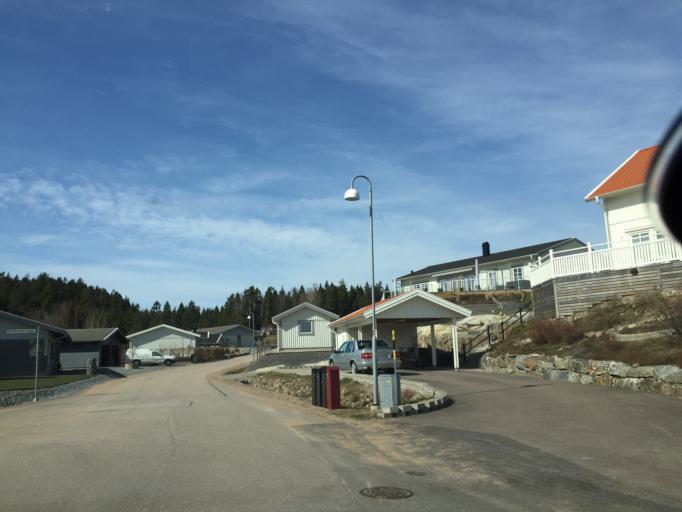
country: SE
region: Vaestra Goetaland
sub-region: Orust
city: Henan
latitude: 58.3436
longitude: 11.7322
